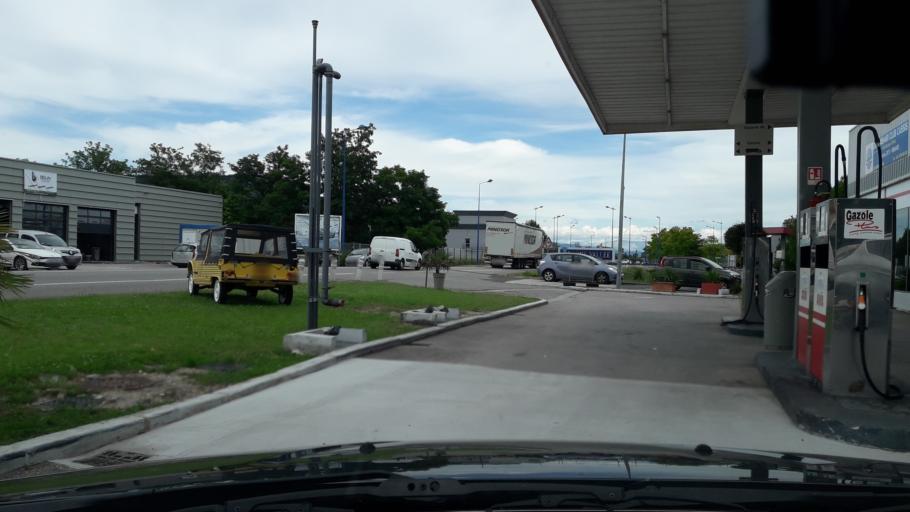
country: FR
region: Rhone-Alpes
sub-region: Departement de l'Ardeche
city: Le Pouzin
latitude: 44.7561
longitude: 4.7581
